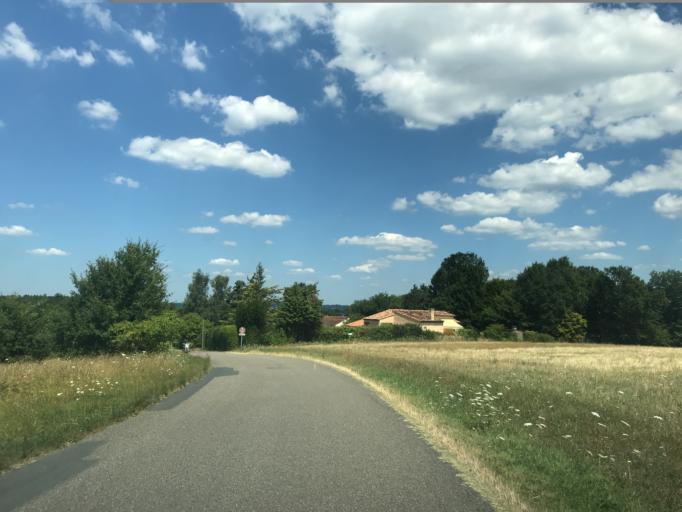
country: FR
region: Aquitaine
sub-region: Departement de la Dordogne
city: Sarlat-la-Caneda
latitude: 44.8476
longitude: 1.2033
